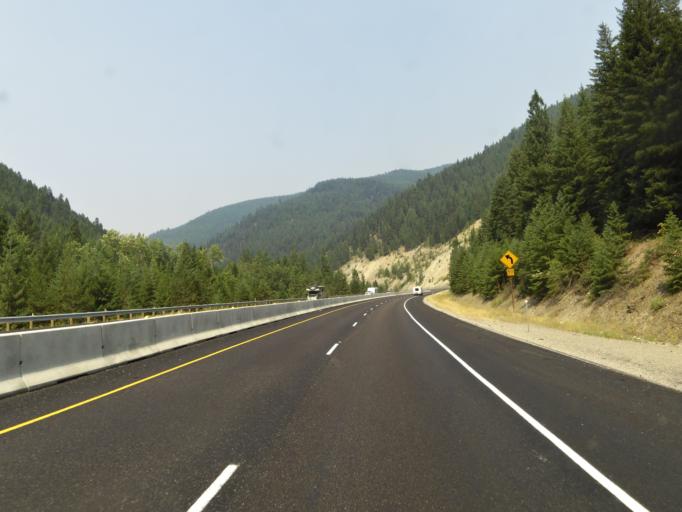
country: US
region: Montana
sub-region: Sanders County
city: Thompson Falls
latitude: 47.3083
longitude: -115.2073
